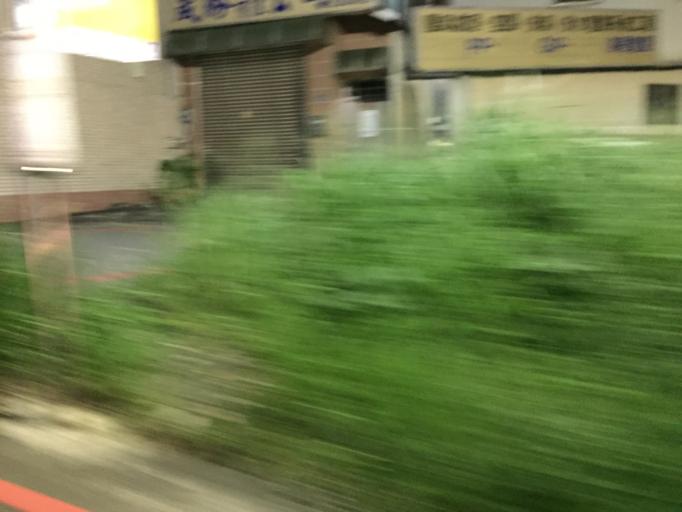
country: TW
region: Taiwan
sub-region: Hsinchu
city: Hsinchu
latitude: 24.7717
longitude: 120.9681
